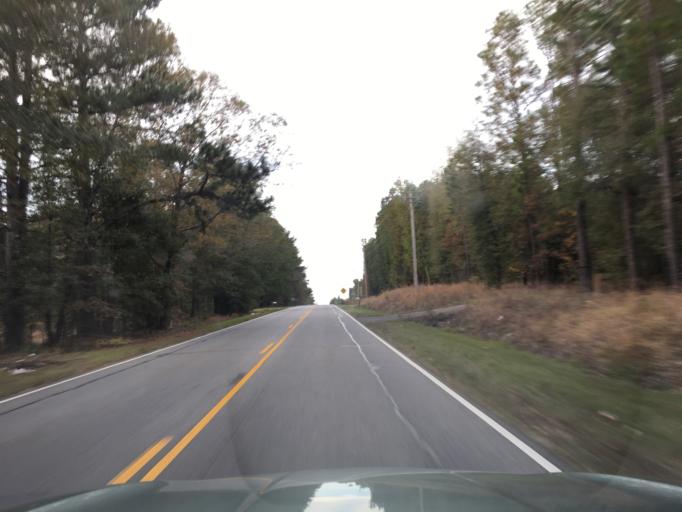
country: US
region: South Carolina
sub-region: Lexington County
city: Leesville
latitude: 33.8125
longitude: -81.4476
